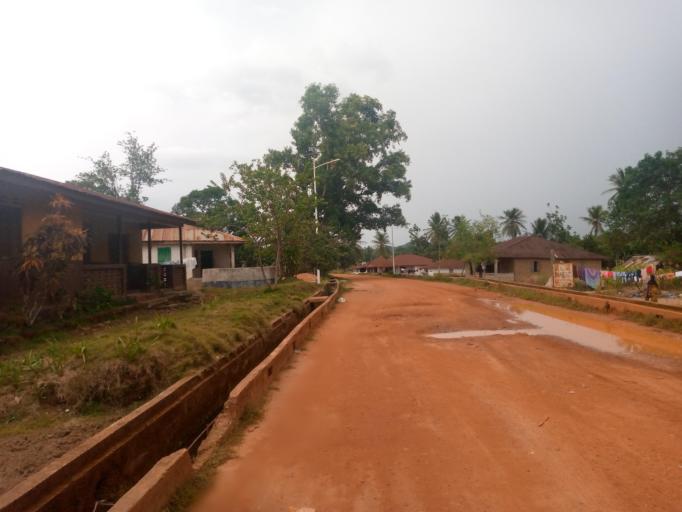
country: SL
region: Southern Province
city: Mogbwemo
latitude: 7.6069
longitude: -12.1743
